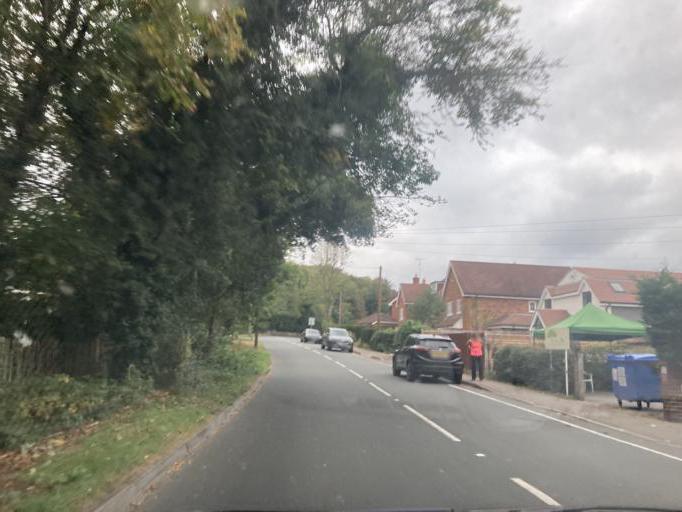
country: GB
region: England
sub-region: Surrey
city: Windlesham
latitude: 51.3725
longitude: -0.6720
